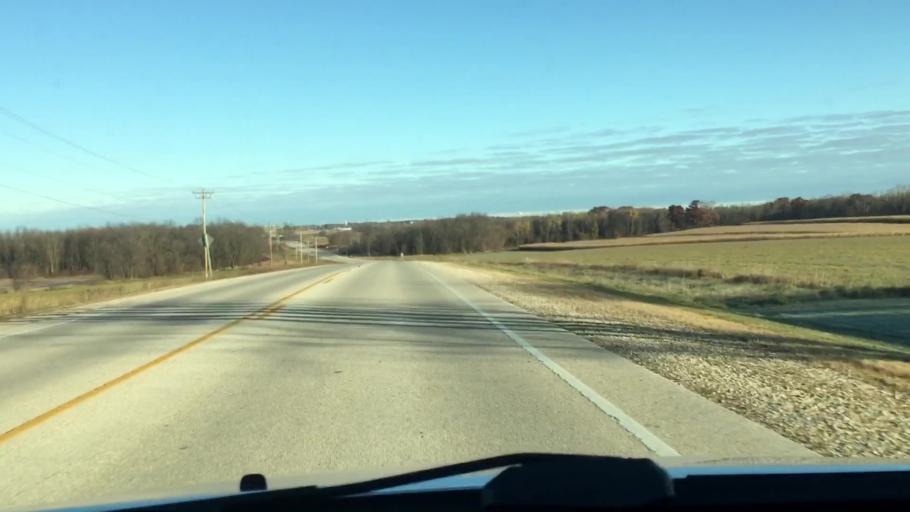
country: US
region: Wisconsin
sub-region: Dodge County
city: Theresa
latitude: 43.5528
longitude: -88.4436
